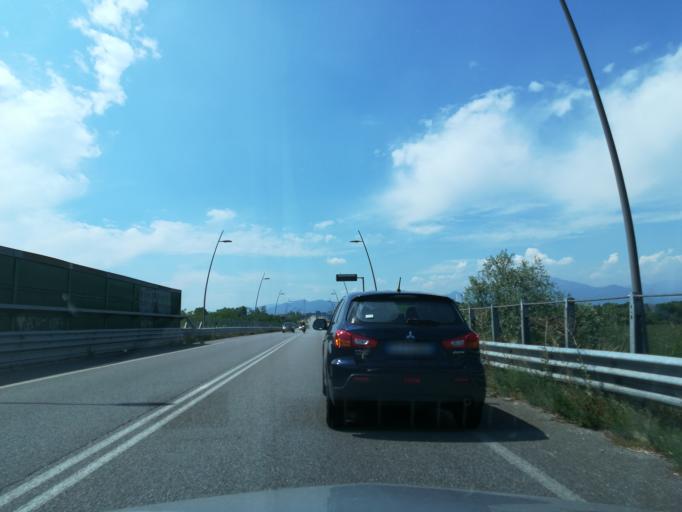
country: IT
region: Lombardy
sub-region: Provincia di Bergamo
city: Stezzano
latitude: 45.6420
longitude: 9.6359
